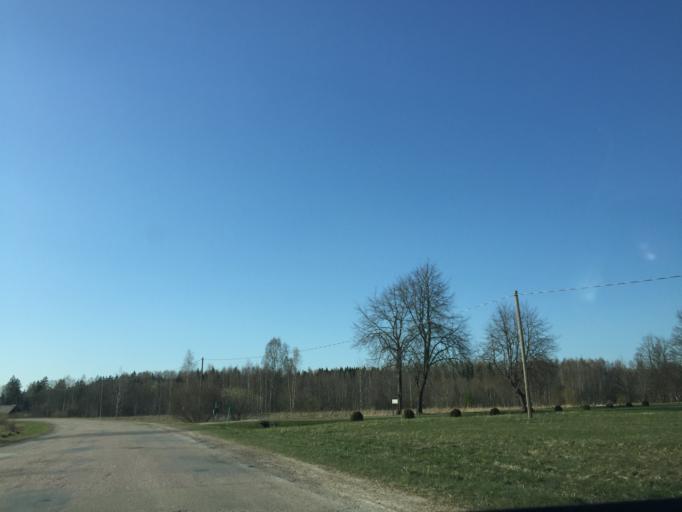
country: LV
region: Ropazu
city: Ropazi
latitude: 56.9671
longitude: 24.6784
